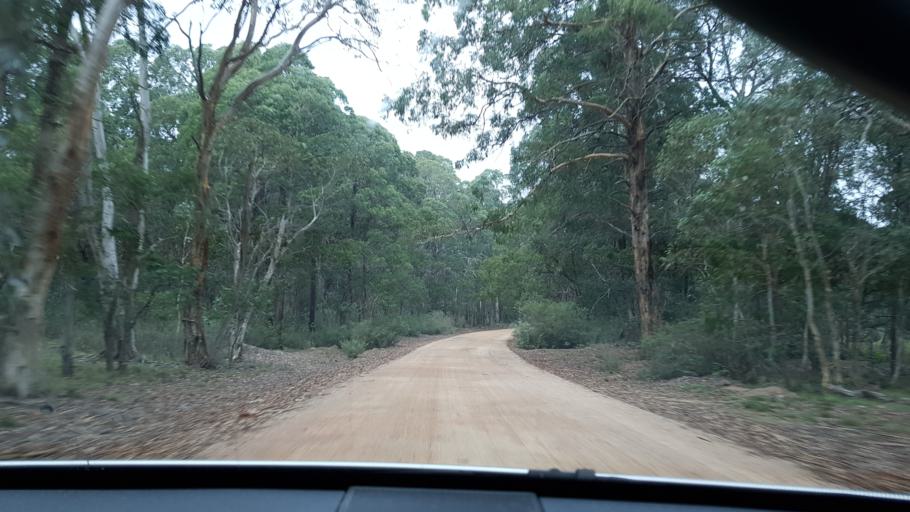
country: AU
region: New South Wales
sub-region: Oberon
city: Oberon
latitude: -33.9725
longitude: 150.0568
